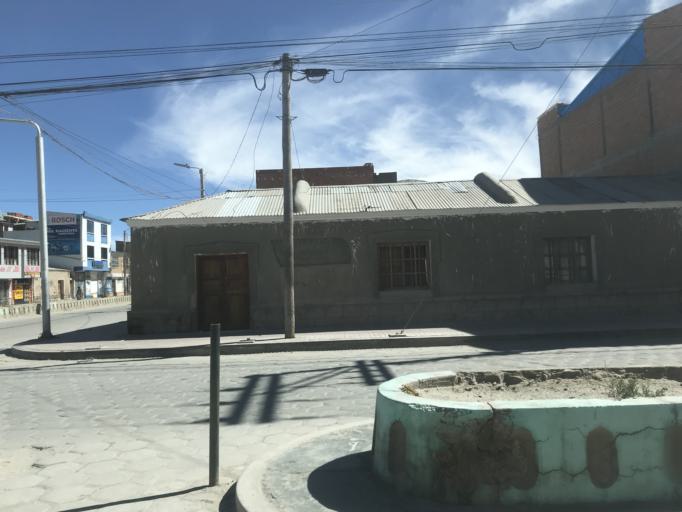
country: BO
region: Potosi
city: Uyuni
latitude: -20.4611
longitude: -66.8240
